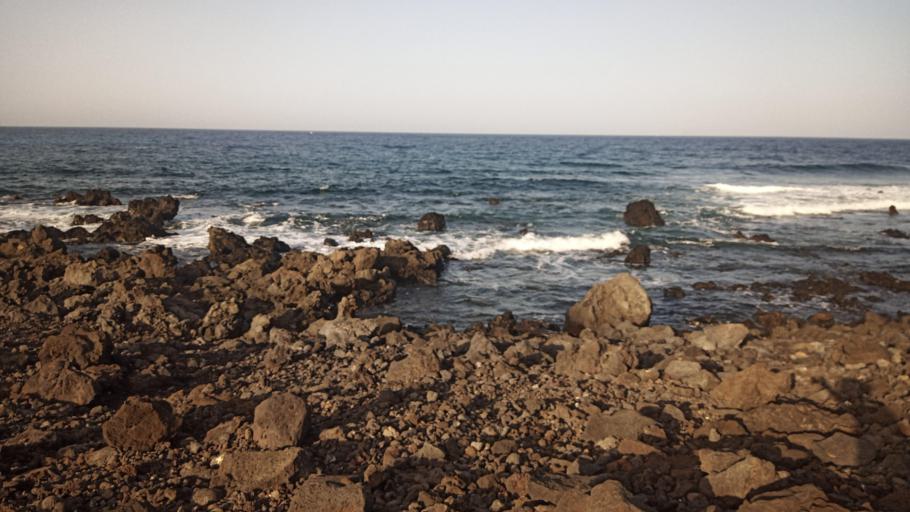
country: ES
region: Canary Islands
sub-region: Provincia de Las Palmas
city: Haria
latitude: 29.2089
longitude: -13.4268
